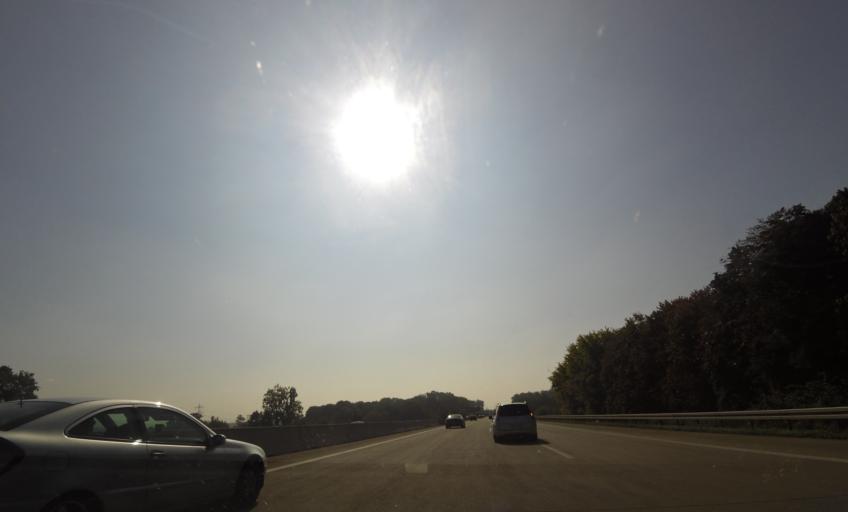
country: DE
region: Baden-Wuerttemberg
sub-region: Freiburg Region
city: Achern
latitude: 48.6387
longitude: 8.0264
